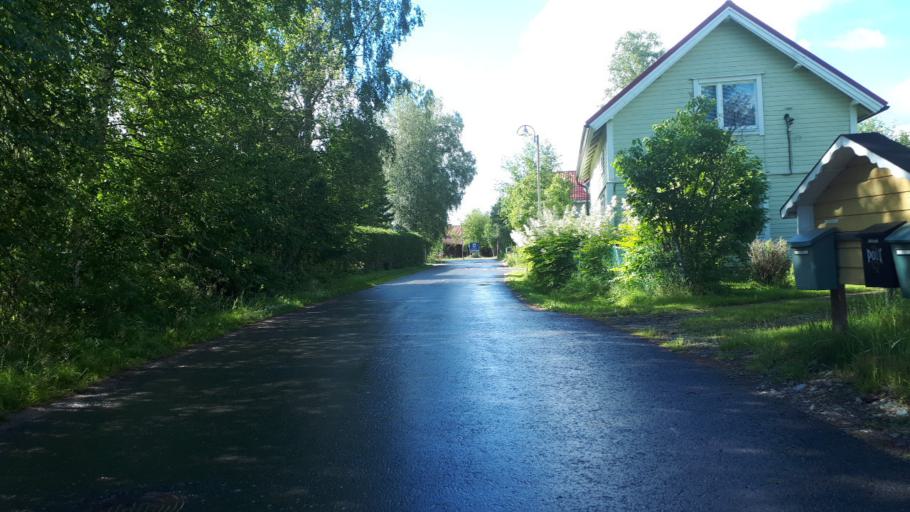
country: FI
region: Northern Ostrobothnia
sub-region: Oulunkaari
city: Ii
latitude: 65.3253
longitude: 25.3763
